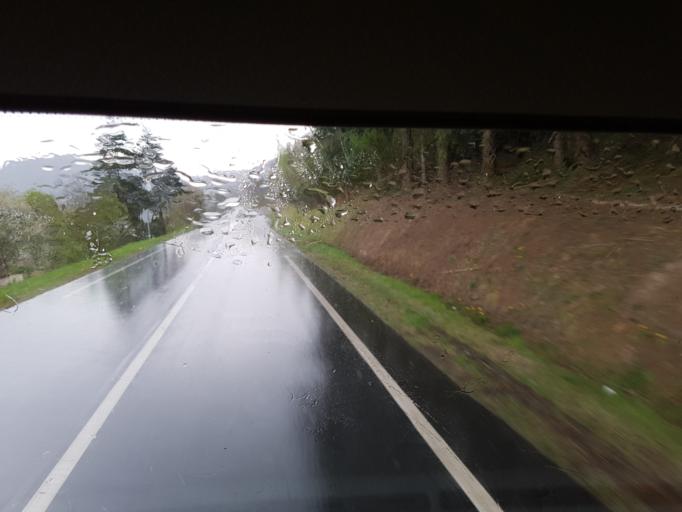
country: FR
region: Auvergne
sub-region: Departement de la Haute-Loire
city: Aurec-sur-Loire
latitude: 45.3749
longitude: 4.2150
